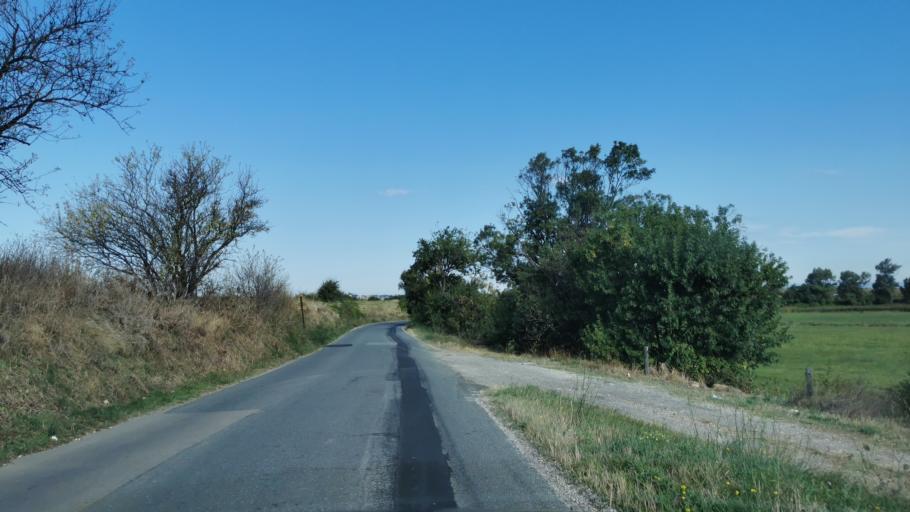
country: FR
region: Languedoc-Roussillon
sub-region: Departement de l'Aude
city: Narbonne
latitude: 43.1437
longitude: 3.0163
